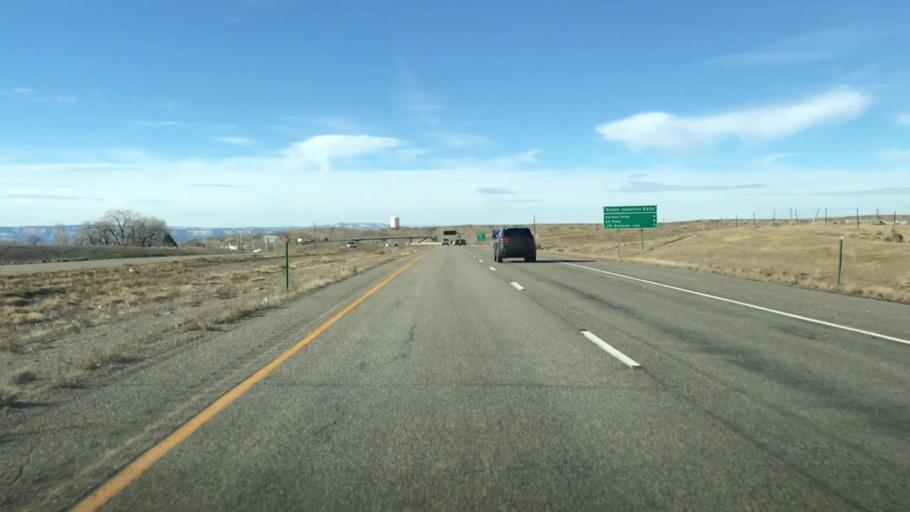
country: US
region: Colorado
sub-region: Mesa County
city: Clifton
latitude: 39.1077
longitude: -108.4324
